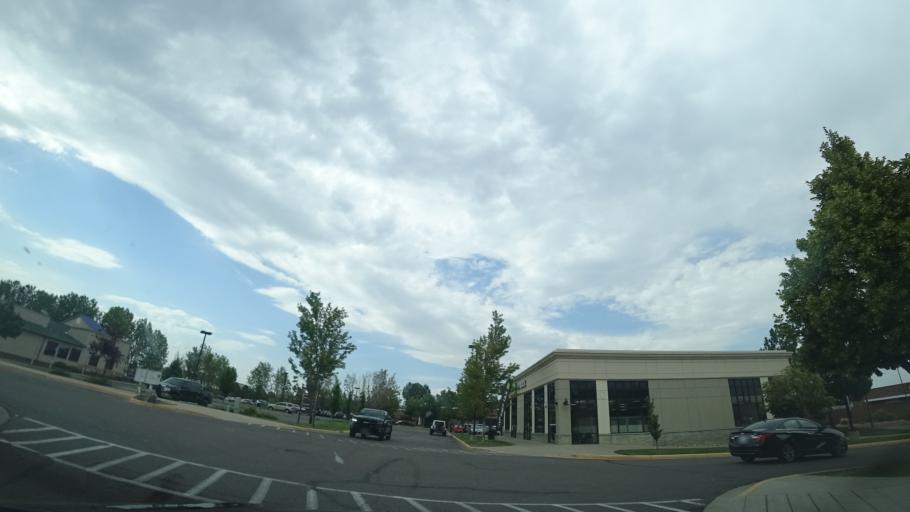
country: US
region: Colorado
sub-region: Jefferson County
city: Lakewood
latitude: 39.7091
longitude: -105.0822
